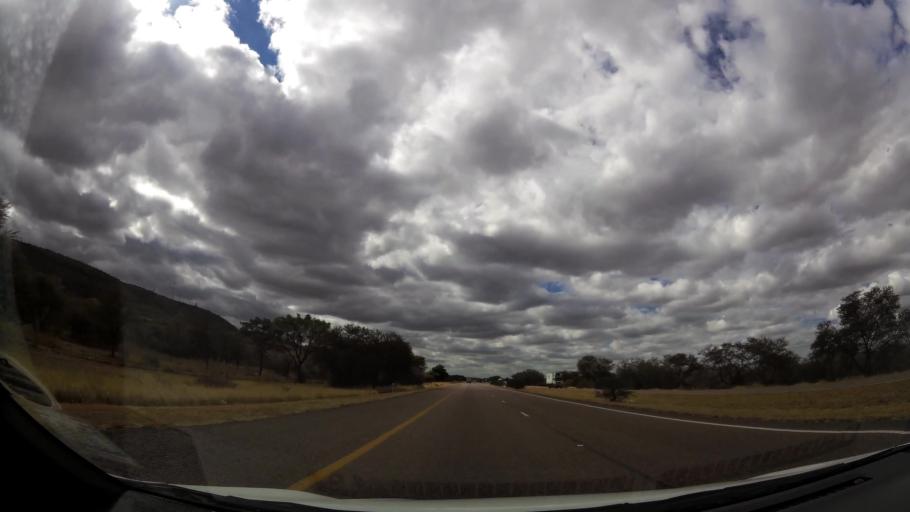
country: ZA
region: Limpopo
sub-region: Waterberg District Municipality
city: Modimolle
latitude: -24.8157
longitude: 28.4298
